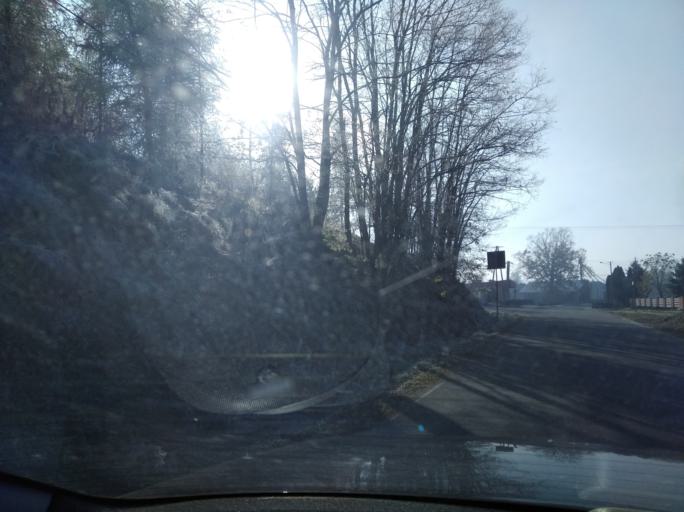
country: PL
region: Subcarpathian Voivodeship
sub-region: Powiat strzyzowski
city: Wysoka Strzyzowska
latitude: 49.8637
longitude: 21.7084
